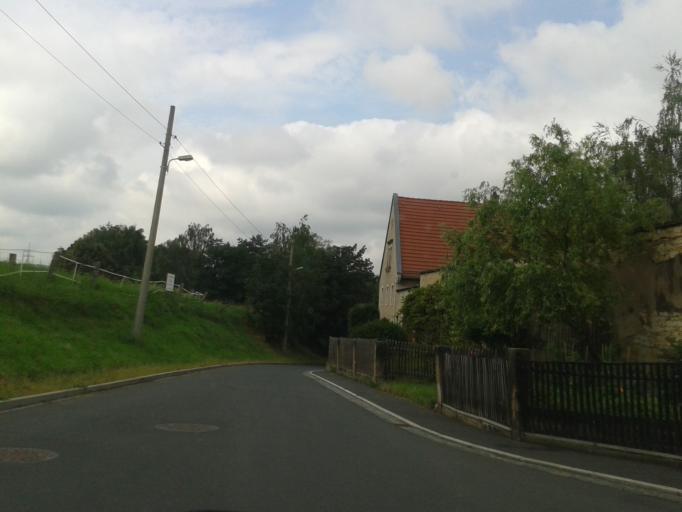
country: DE
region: Saxony
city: Bannewitz
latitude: 51.0094
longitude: 13.7505
